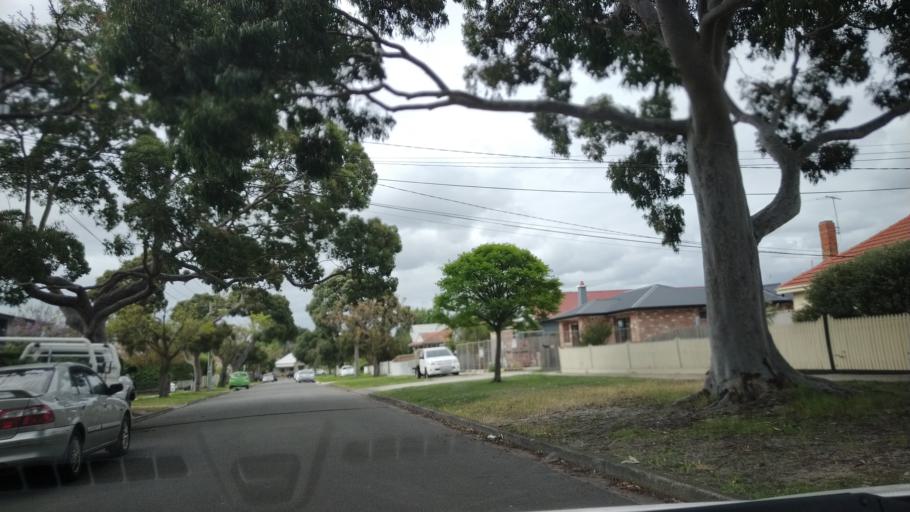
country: AU
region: Victoria
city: Hughesdale
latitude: -37.8987
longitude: 145.0803
